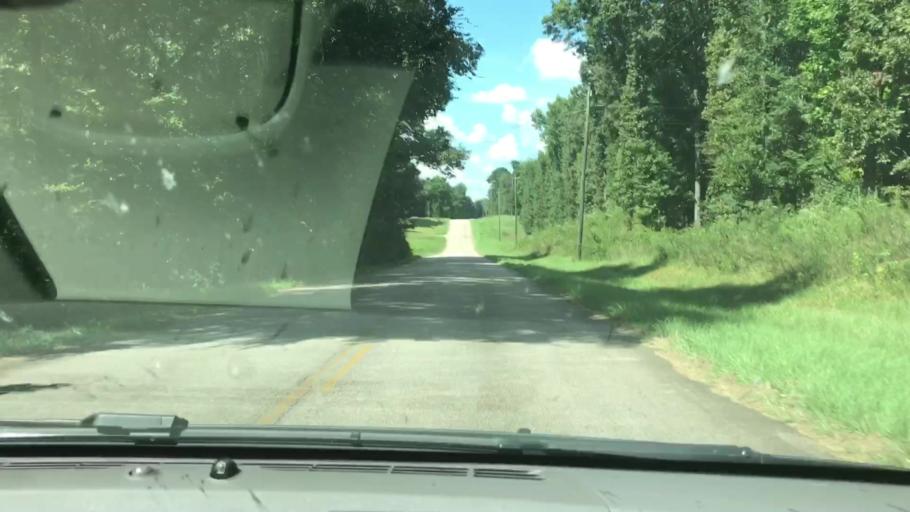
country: US
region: Georgia
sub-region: Troup County
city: La Grange
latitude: 33.0943
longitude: -85.1297
